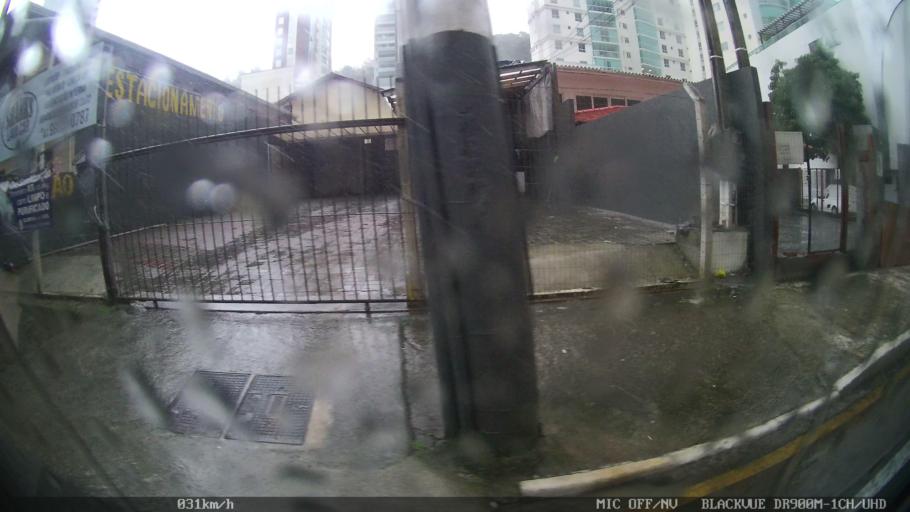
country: BR
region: Santa Catarina
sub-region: Balneario Camboriu
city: Balneario Camboriu
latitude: -26.9700
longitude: -48.6350
